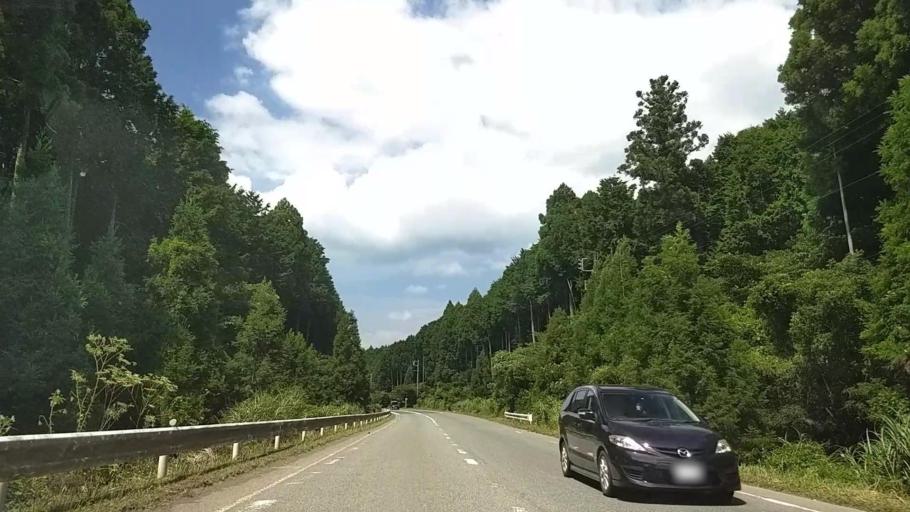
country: JP
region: Shizuoka
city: Fuji
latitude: 35.2452
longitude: 138.7159
